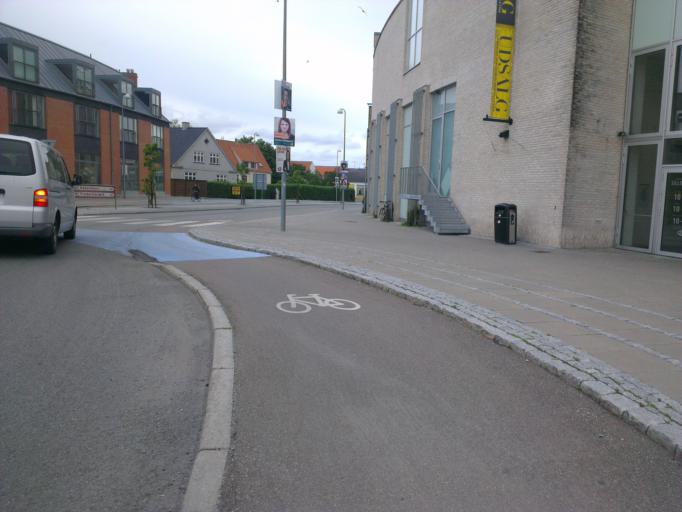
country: DK
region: Capital Region
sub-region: Frederikssund Kommune
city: Frederikssund
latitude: 55.8357
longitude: 12.0631
